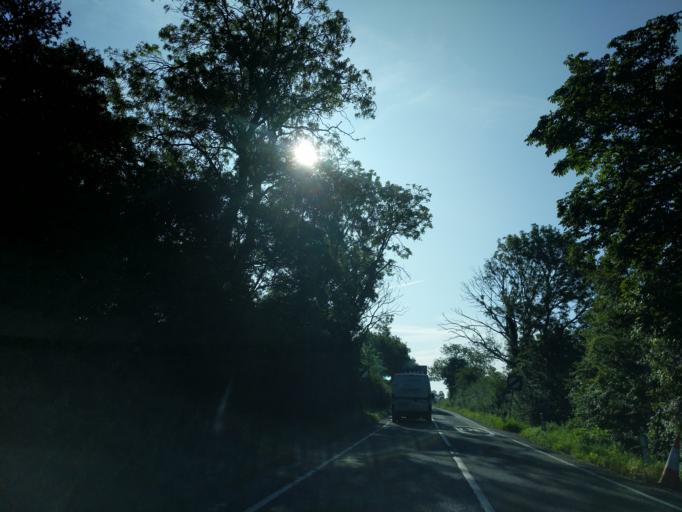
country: GB
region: England
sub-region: District of Rutland
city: Clipsham
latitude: 52.8097
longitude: -0.5127
